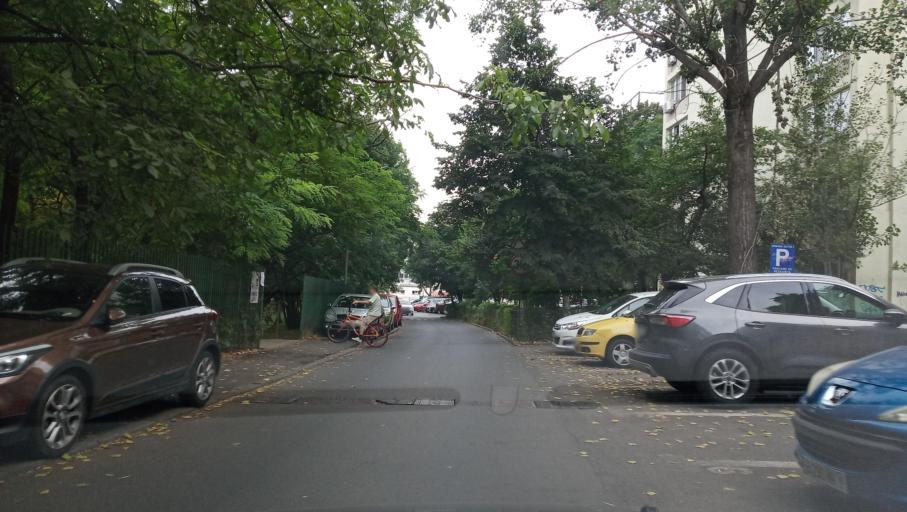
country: RO
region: Ilfov
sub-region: Comuna Popesti-Leordeni
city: Popesti-Leordeni
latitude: 44.4202
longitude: 26.1607
